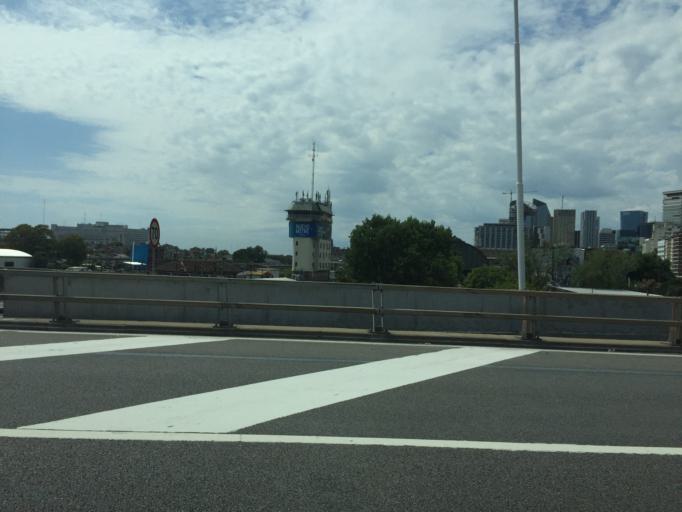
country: AR
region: Buenos Aires F.D.
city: Retiro
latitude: -34.5881
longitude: -58.3811
